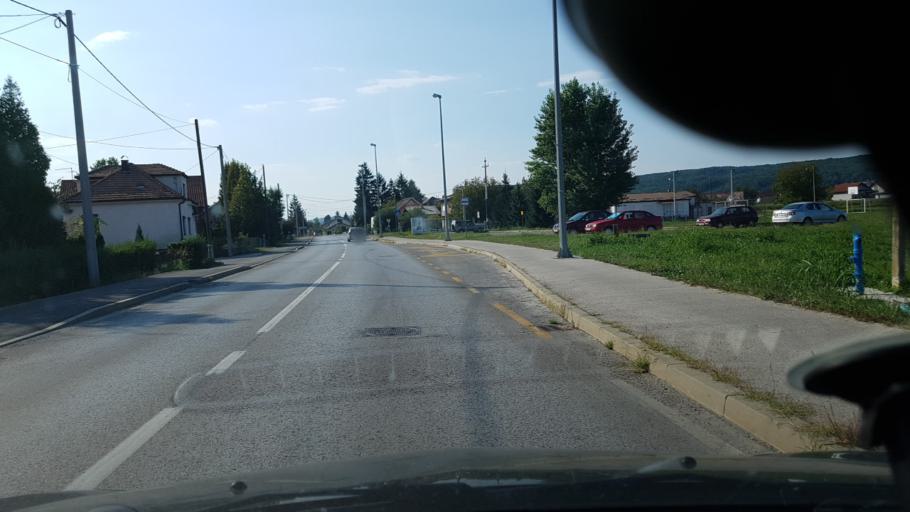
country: HR
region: Zagrebacka
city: Brdovec
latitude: 45.8624
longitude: 15.7753
